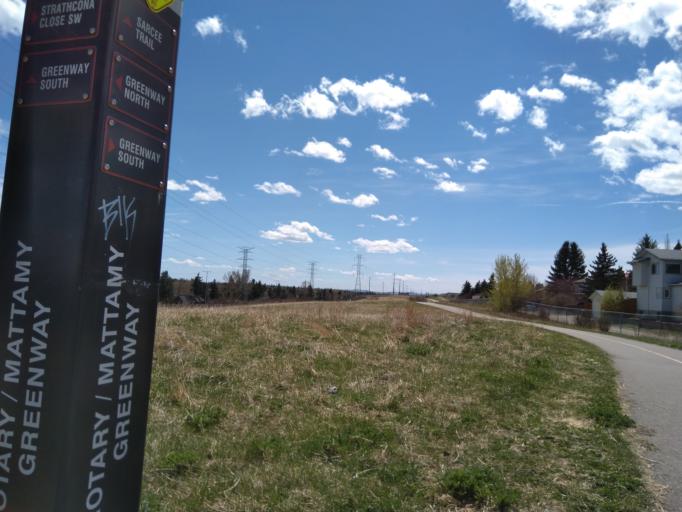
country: CA
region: Alberta
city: Calgary
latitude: 51.0480
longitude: -114.1653
